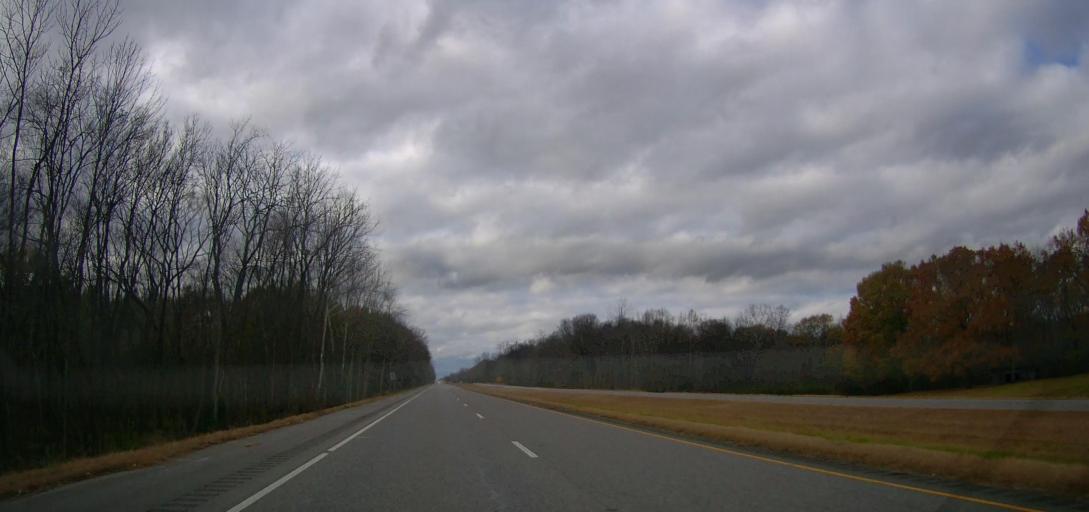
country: US
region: Alabama
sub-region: Lawrence County
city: Town Creek
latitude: 34.6293
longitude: -87.4822
